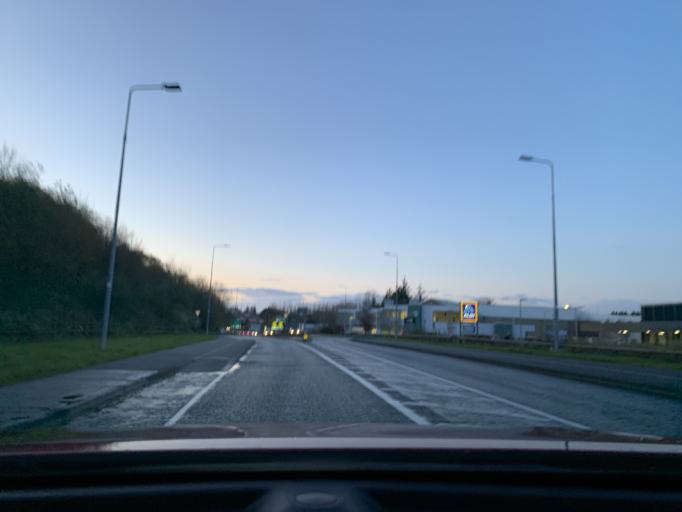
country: IE
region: Connaught
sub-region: County Leitrim
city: Carrick-on-Shannon
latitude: 53.9450
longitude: -8.0741
